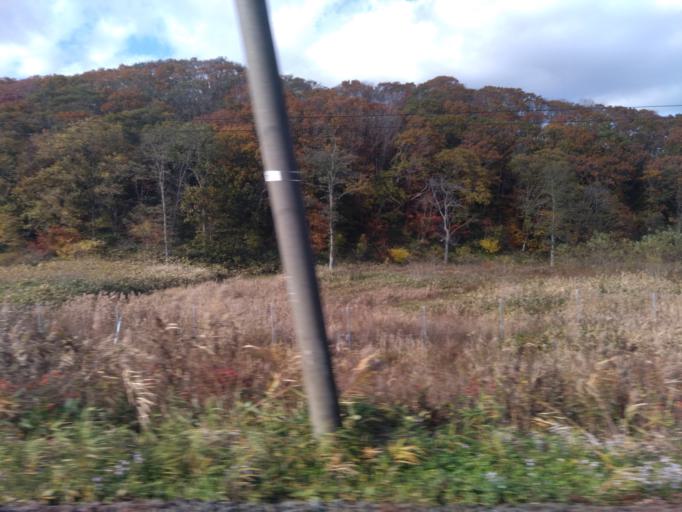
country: JP
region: Hokkaido
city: Shiraoi
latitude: 42.5664
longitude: 141.3805
